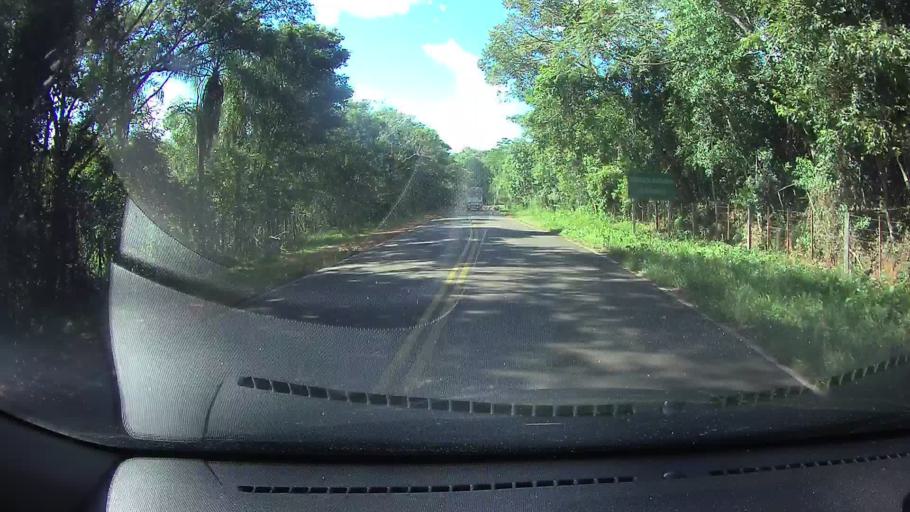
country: PY
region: Paraguari
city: Sapucai
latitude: -25.6667
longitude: -56.8576
